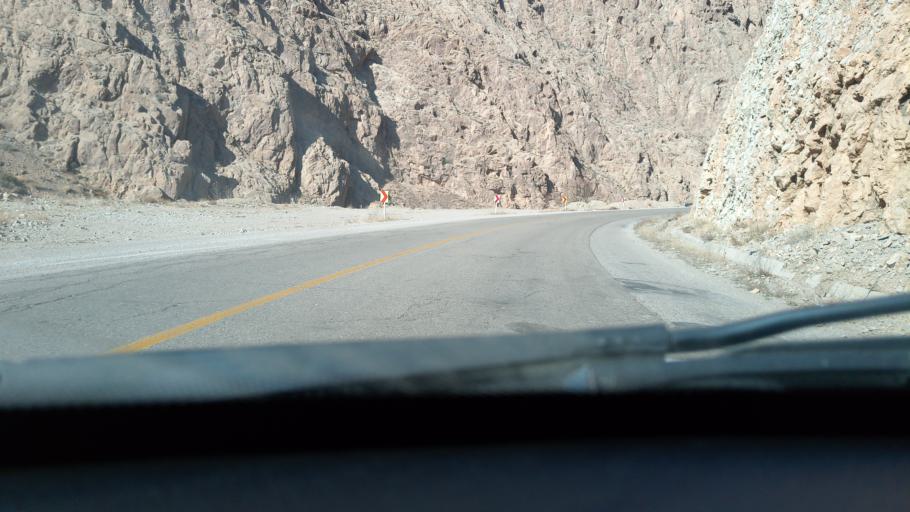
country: IR
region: Khorasan-e Shomali
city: Esfarayen
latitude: 37.1775
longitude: 57.4138
